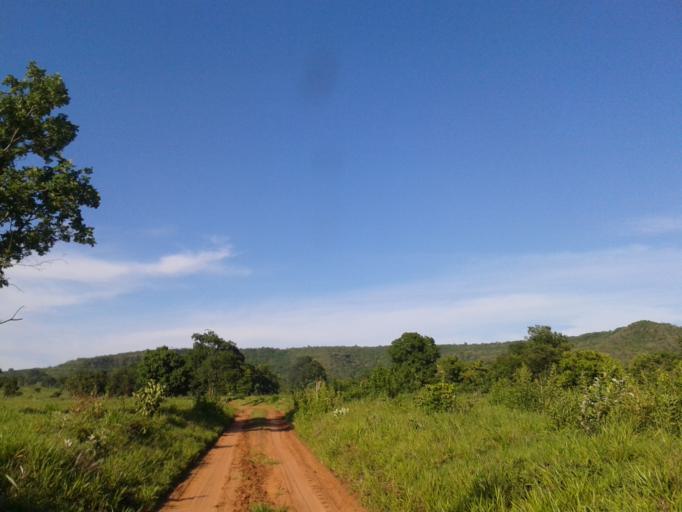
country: BR
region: Minas Gerais
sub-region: Santa Vitoria
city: Santa Vitoria
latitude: -19.0824
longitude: -49.9589
